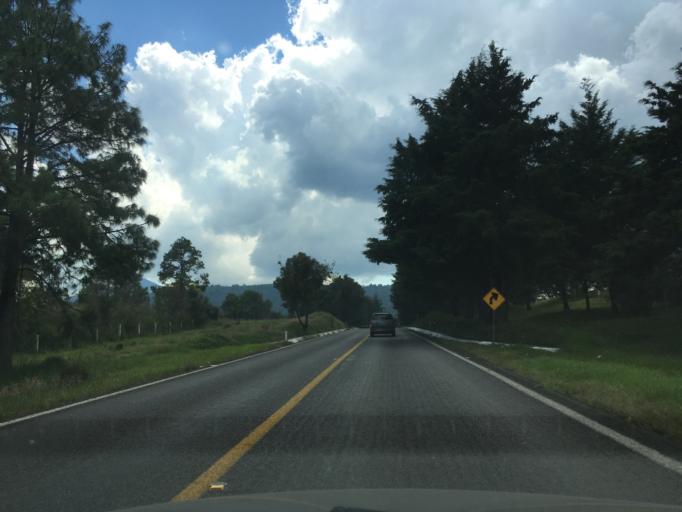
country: MX
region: Michoacan
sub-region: Patzcuaro
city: Santa Ana Chapitiro
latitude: 19.5159
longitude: -101.6666
